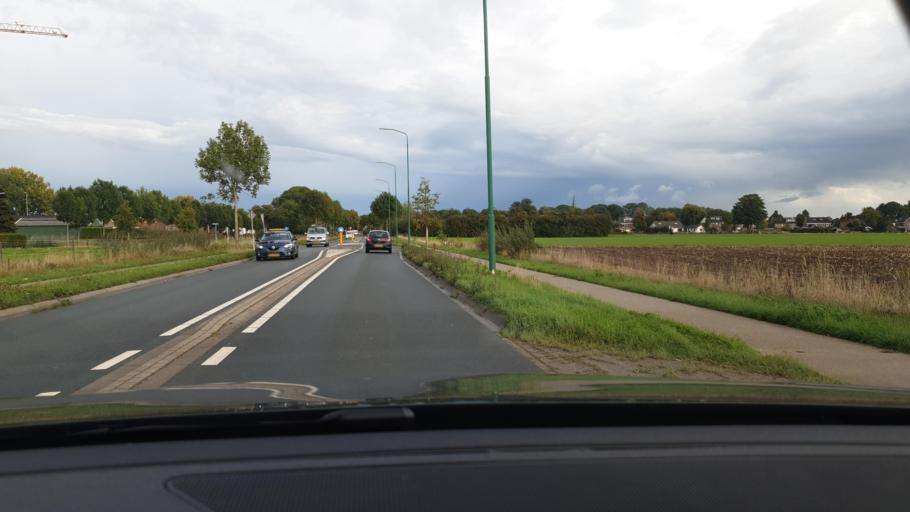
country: NL
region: North Brabant
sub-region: Gemeente Oss
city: Berghem
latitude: 51.8015
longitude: 5.5753
